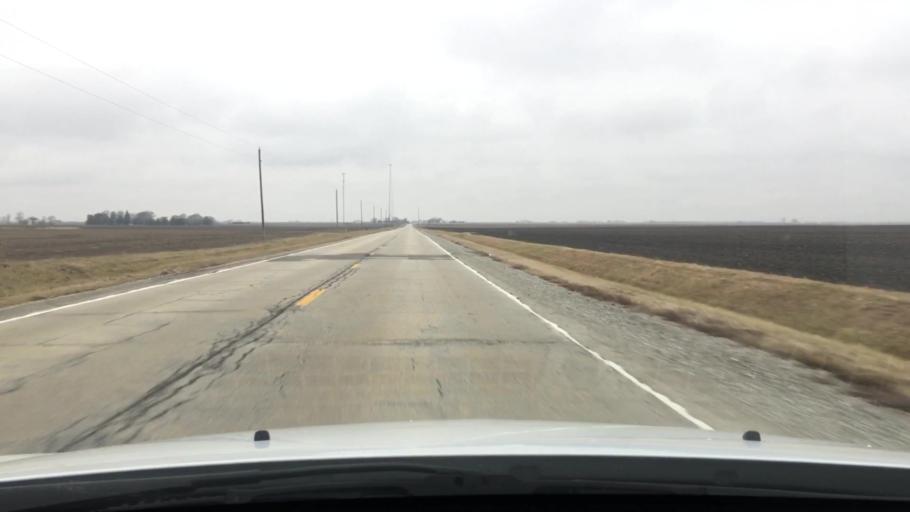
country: US
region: Illinois
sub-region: Iroquois County
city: Clifton
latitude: 40.8836
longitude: -87.9867
